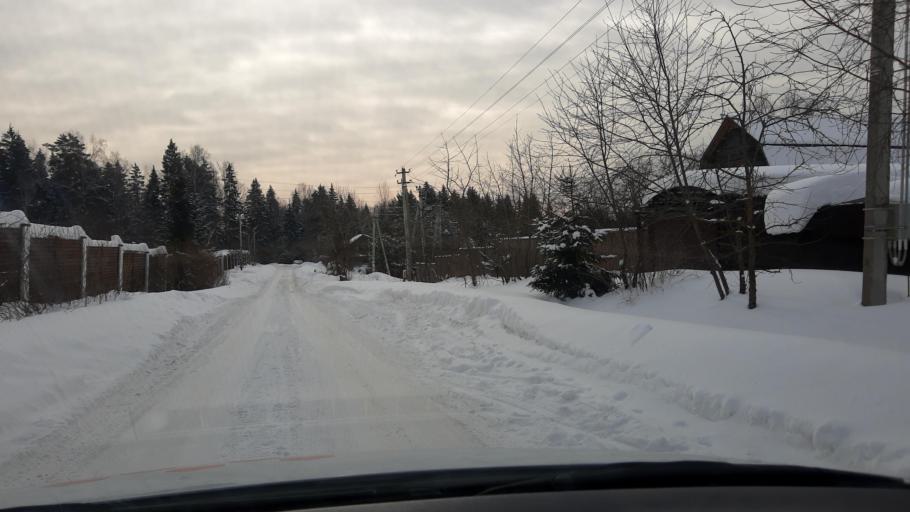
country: RU
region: Moskovskaya
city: Rumyantsevo
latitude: 55.9127
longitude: 36.5802
